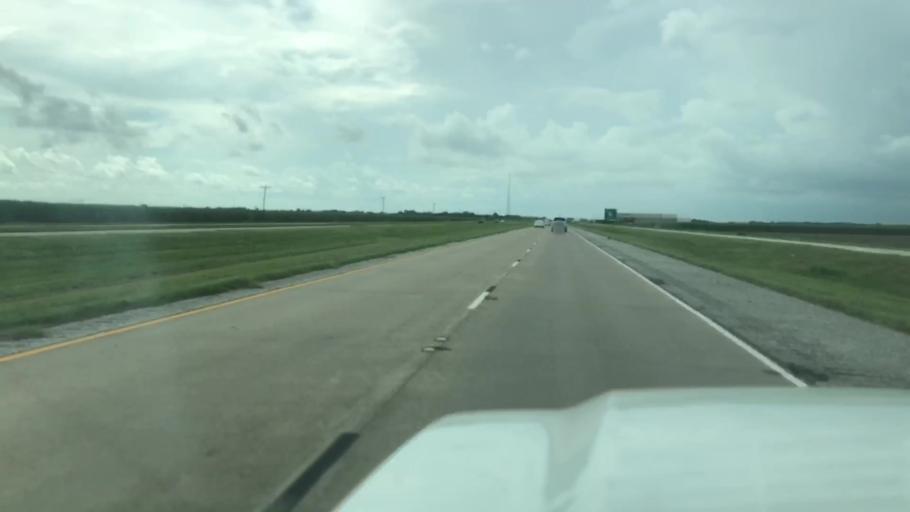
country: US
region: Louisiana
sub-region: Iberia Parish
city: Jeanerette
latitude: 29.9067
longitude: -91.7088
